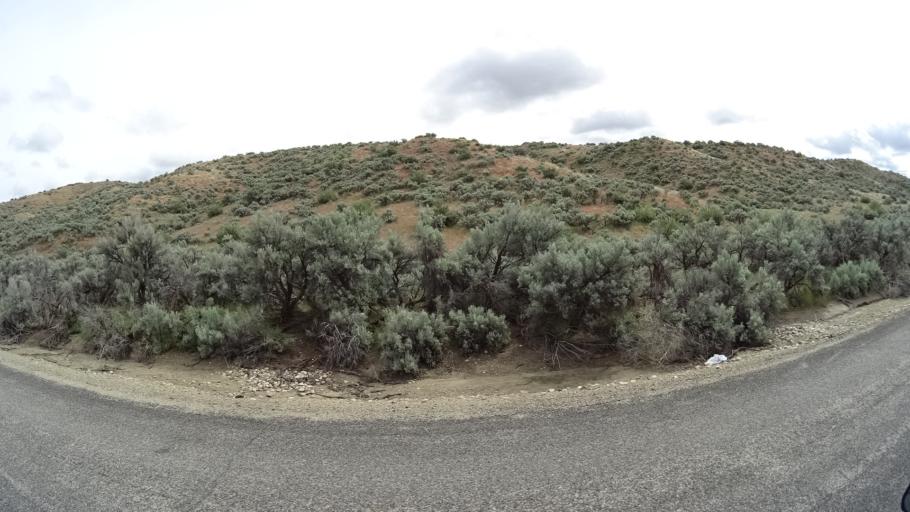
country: US
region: Idaho
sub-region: Ada County
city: Eagle
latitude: 43.7527
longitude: -116.3619
